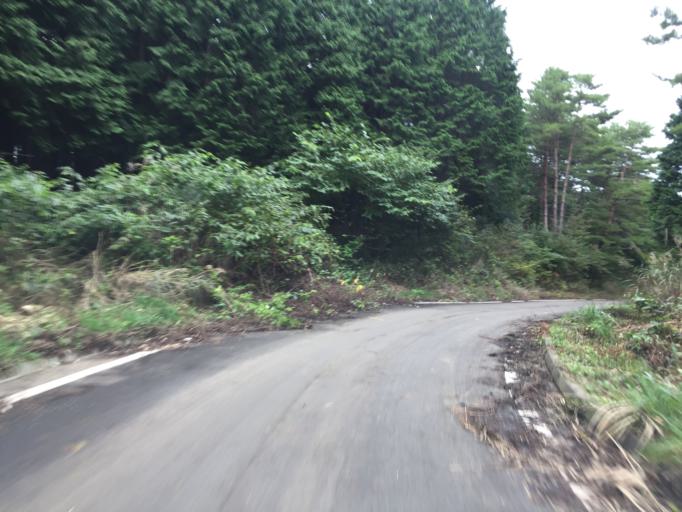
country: JP
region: Miyagi
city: Marumori
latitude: 37.9151
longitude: 140.7111
